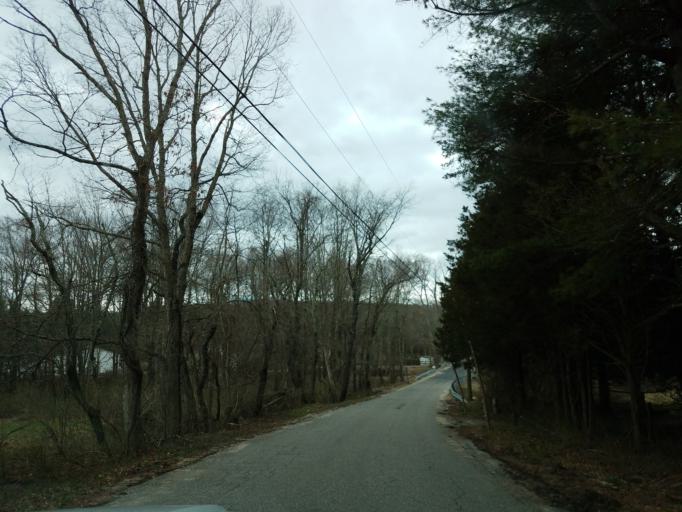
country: US
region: Connecticut
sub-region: Tolland County
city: Coventry Lake
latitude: 41.7613
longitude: -72.3965
